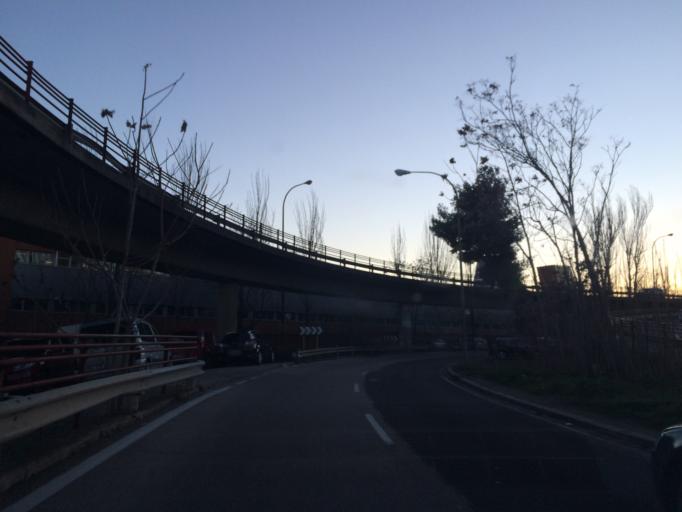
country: ES
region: Madrid
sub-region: Provincia de Madrid
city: Chamartin
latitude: 40.4715
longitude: -3.6797
